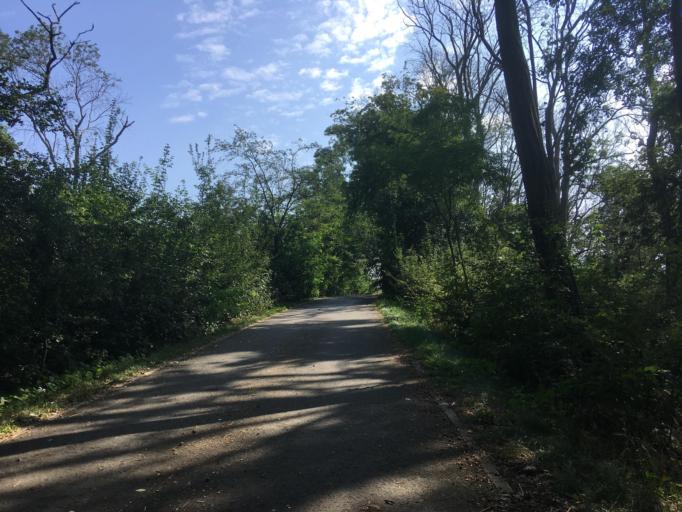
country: DE
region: Saxony
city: Elsnig
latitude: 51.6146
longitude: 12.9434
